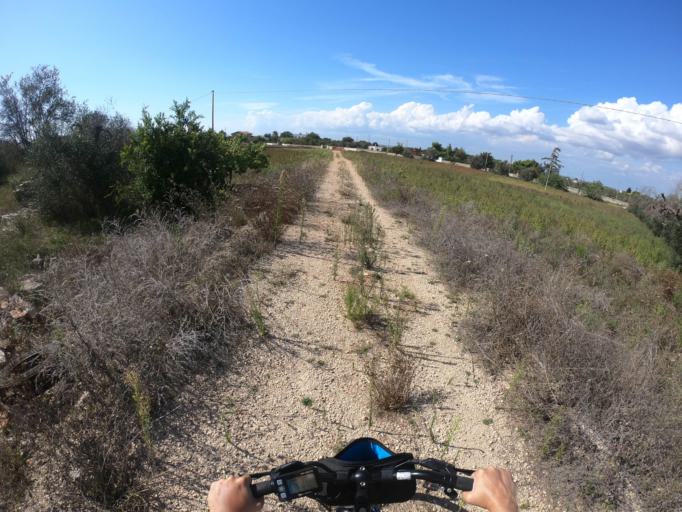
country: IT
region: Apulia
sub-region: Provincia di Lecce
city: Galatone
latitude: 40.1427
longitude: 18.0524
